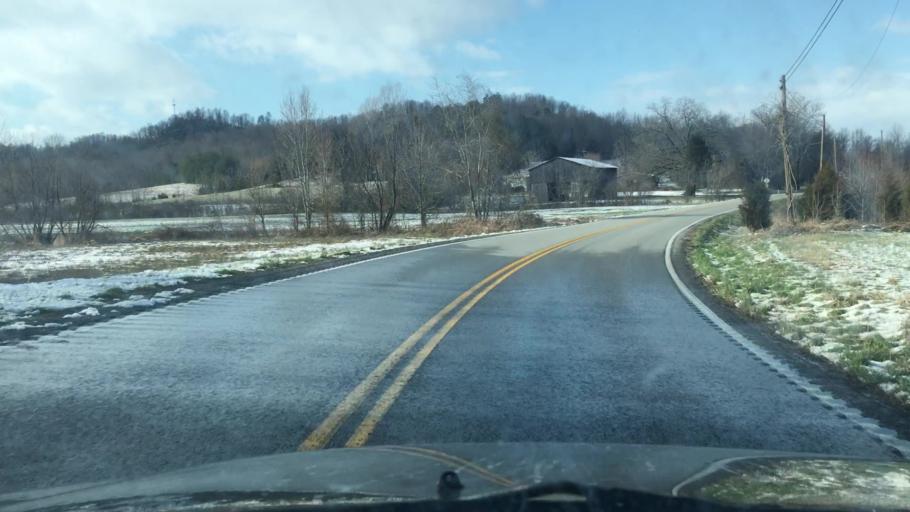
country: US
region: Kentucky
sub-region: Marion County
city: Lebanon
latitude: 37.5225
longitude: -85.3026
